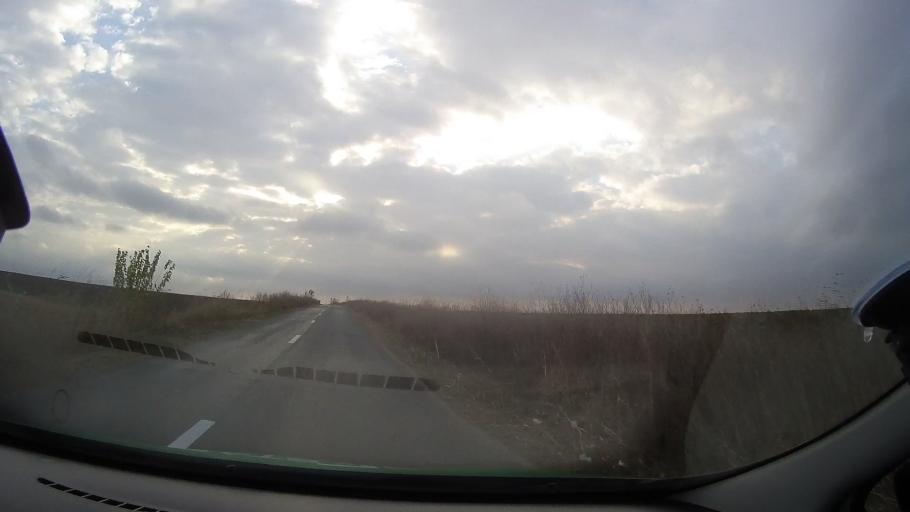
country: RO
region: Constanta
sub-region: Comuna Pestera
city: Pestera
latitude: 44.1320
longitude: 28.1177
